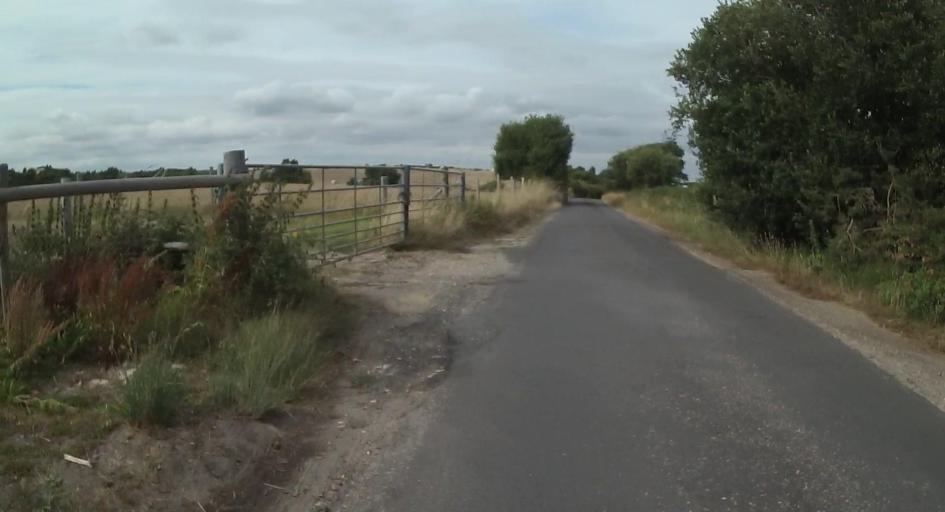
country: GB
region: England
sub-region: Dorset
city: Wareham
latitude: 50.6650
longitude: -2.0855
